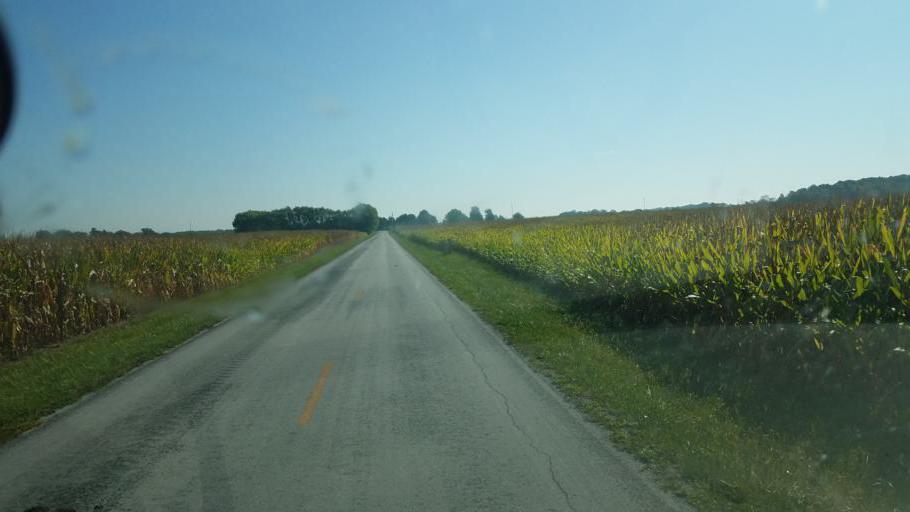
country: US
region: Ohio
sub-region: Hardin County
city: Kenton
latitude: 40.6129
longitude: -83.5740
